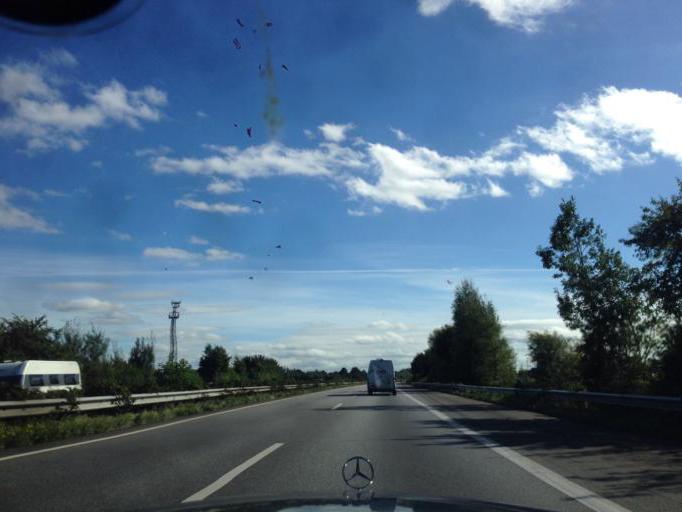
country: DE
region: Schleswig-Holstein
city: Lurschau
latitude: 54.5841
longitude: 9.4655
